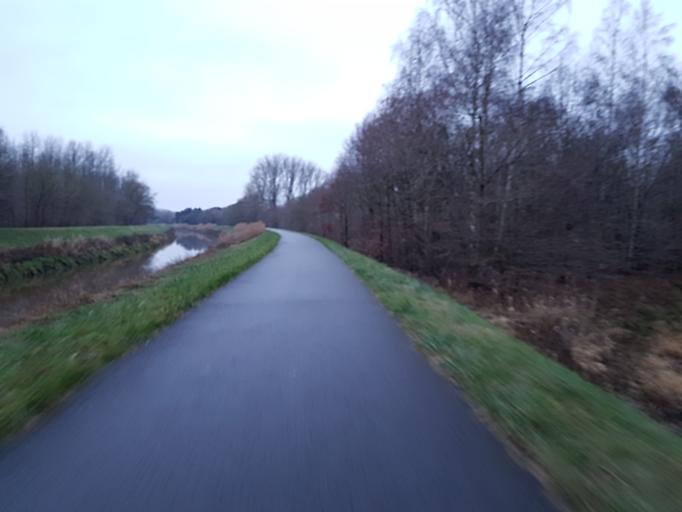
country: BE
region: Flanders
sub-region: Provincie Vlaams-Brabant
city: Rotselaar
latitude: 50.9724
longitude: 4.7370
